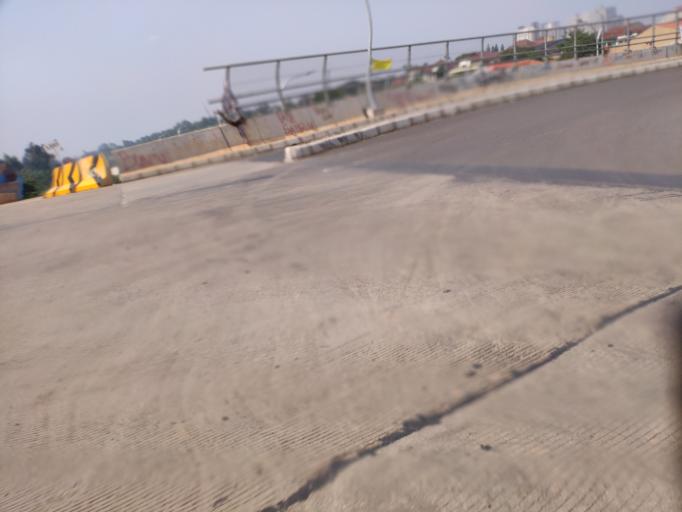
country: ID
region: West Java
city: Pamulang
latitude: -6.3316
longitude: 106.8004
